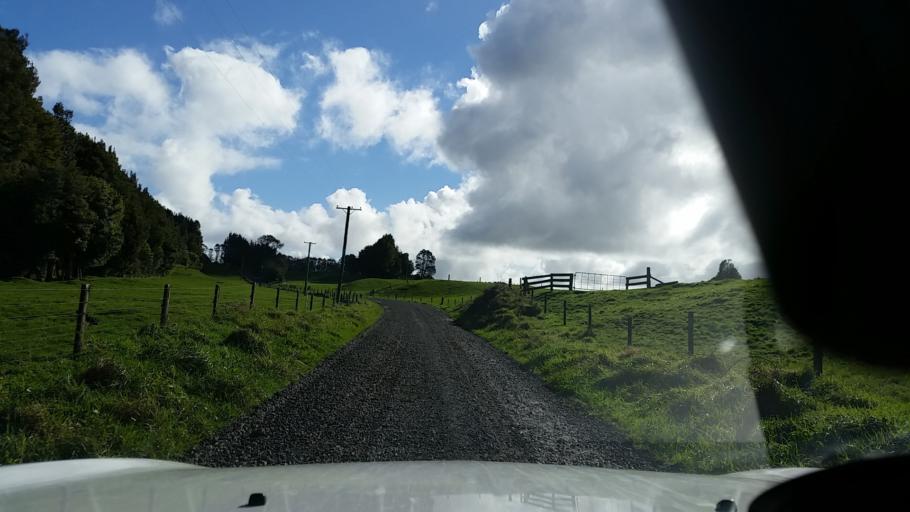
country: NZ
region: Bay of Plenty
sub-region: Rotorua District
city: Rotorua
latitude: -37.9865
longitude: 176.1746
